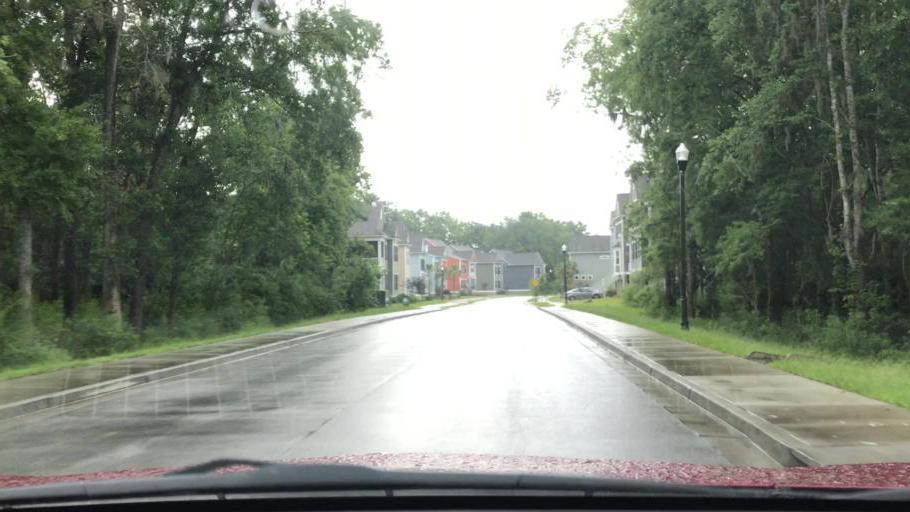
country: US
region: South Carolina
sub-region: Charleston County
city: Shell Point
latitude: 32.8077
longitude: -80.0618
